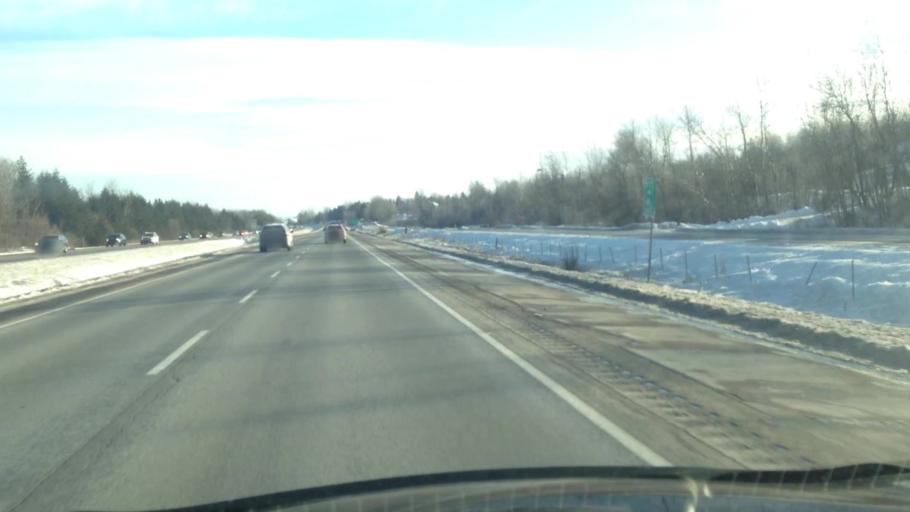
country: CA
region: Quebec
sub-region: Laurentides
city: Prevost
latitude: 45.8205
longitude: -74.0550
